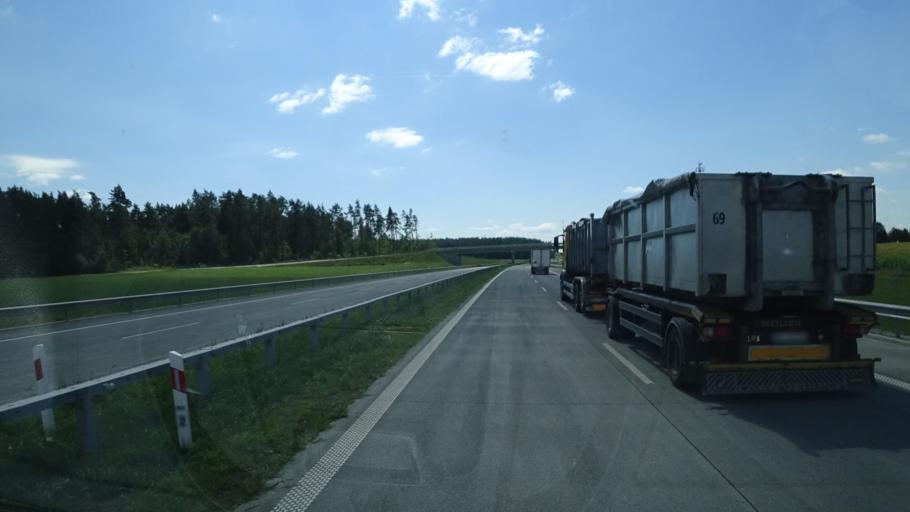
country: PL
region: Podlasie
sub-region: Powiat kolnenski
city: Stawiski
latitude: 53.4676
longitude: 22.2048
